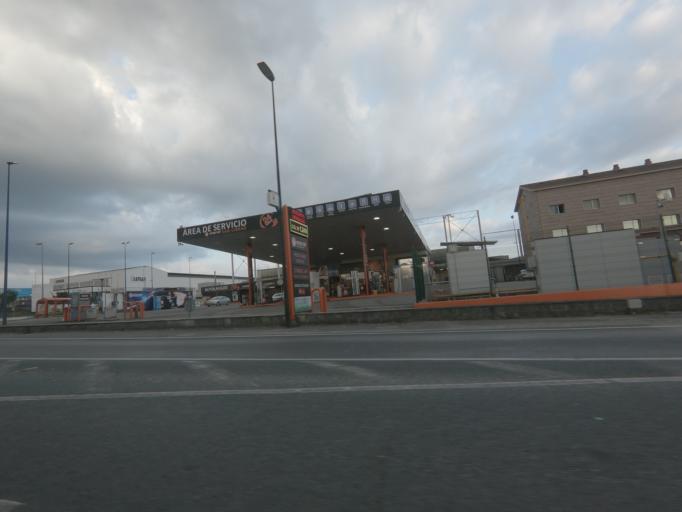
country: ES
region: Galicia
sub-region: Provincia de Ourense
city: Taboadela
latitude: 42.2900
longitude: -7.8169
